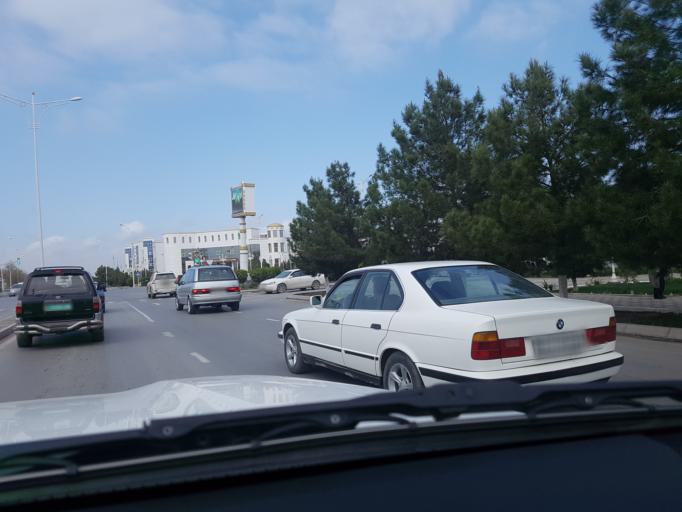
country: TM
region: Lebap
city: Turkmenabat
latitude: 39.0727
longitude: 63.5878
